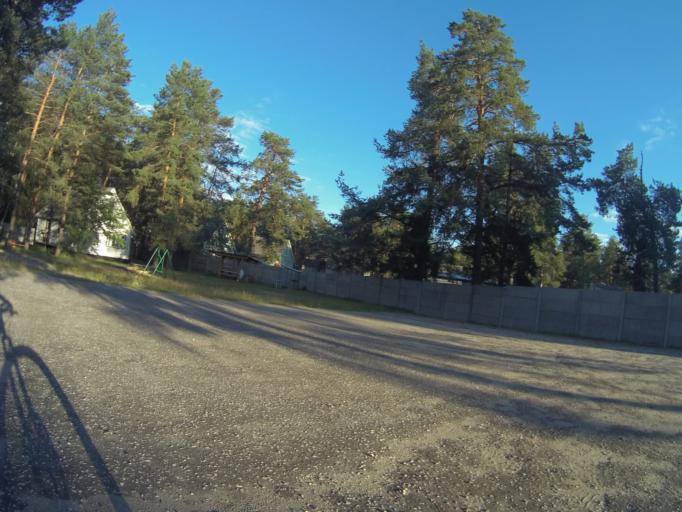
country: RU
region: Vladimir
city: Kommunar
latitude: 56.1417
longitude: 40.4910
